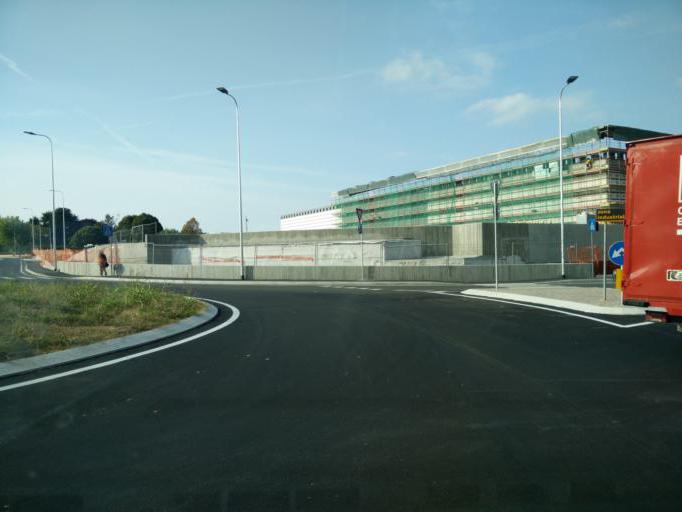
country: IT
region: Lombardy
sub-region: Provincia di Brescia
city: Colombaro-Timoline
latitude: 45.6446
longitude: 10.0122
